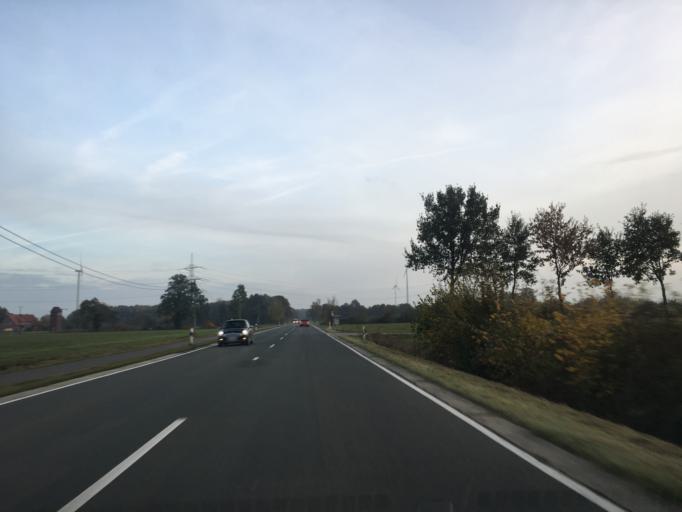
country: DE
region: North Rhine-Westphalia
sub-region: Regierungsbezirk Munster
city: Altenberge
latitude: 52.0842
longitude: 7.4256
